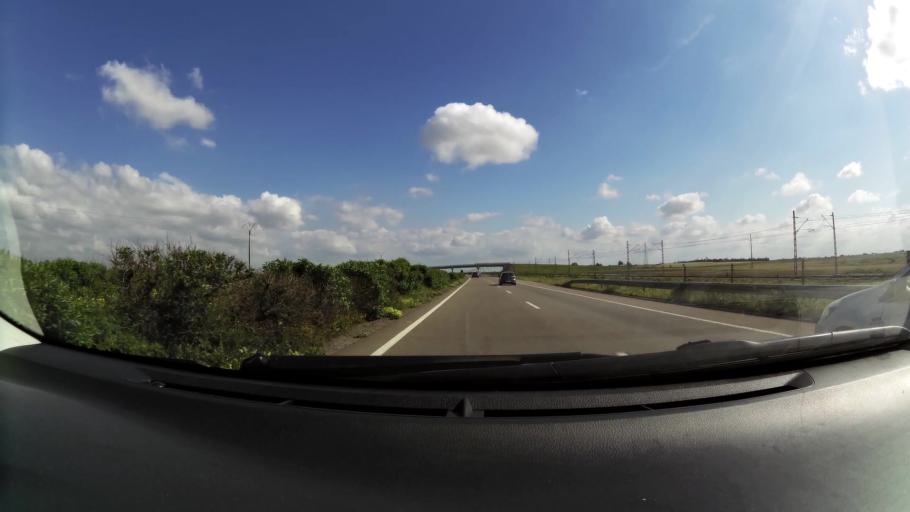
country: MA
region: Chaouia-Ouardigha
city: Nouaseur
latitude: 33.3596
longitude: -7.6188
